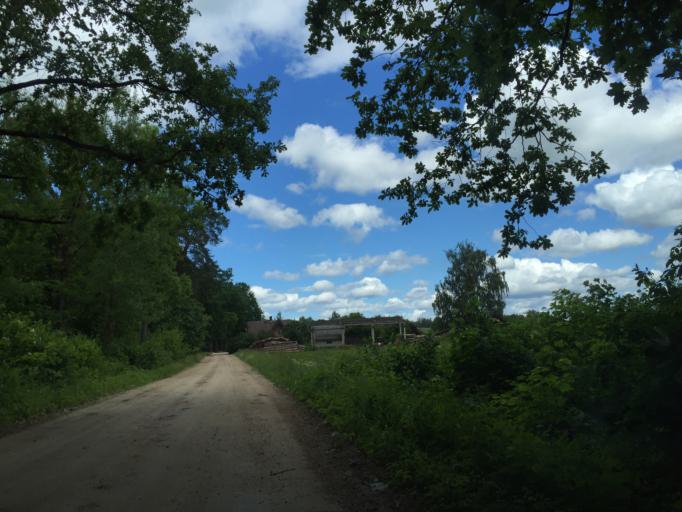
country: LV
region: Lecava
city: Iecava
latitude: 56.5870
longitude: 24.2038
